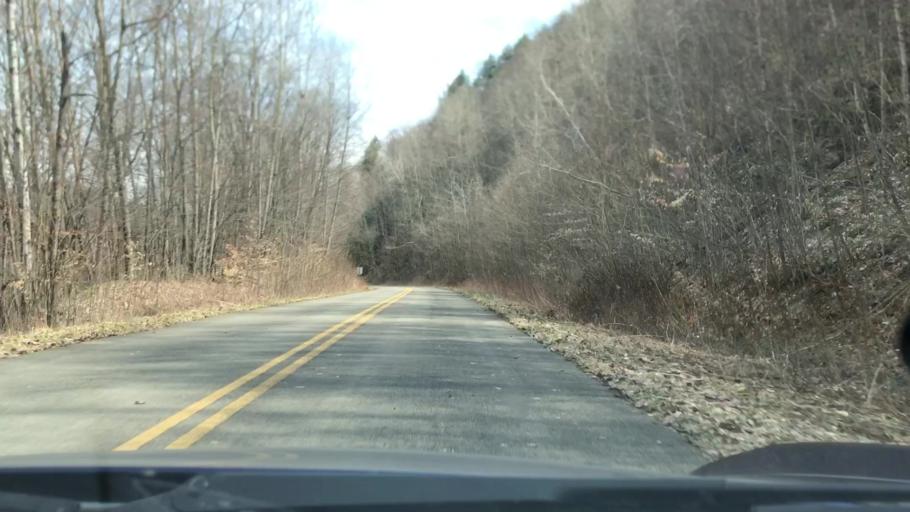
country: US
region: Pennsylvania
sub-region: Warren County
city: Sheffield
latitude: 41.8137
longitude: -78.9468
